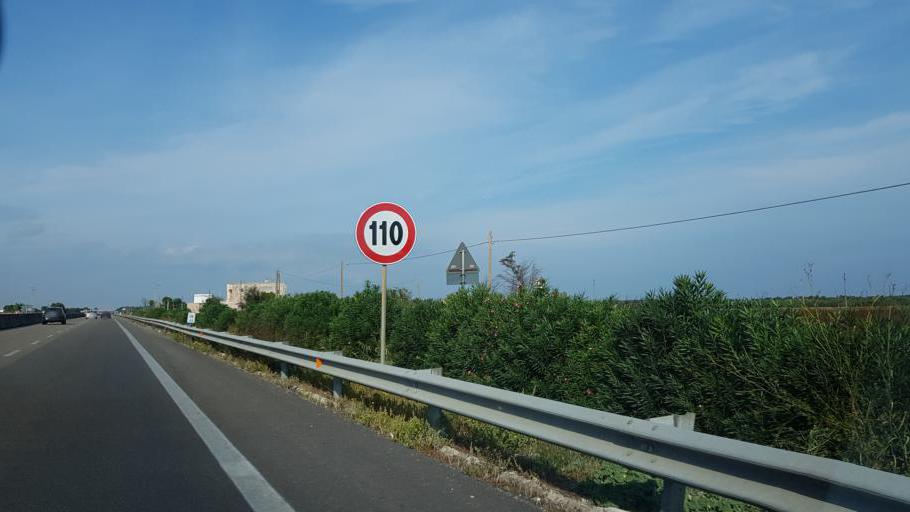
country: IT
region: Apulia
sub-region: Provincia di Brindisi
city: Brindisi
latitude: 40.6782
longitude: 17.8439
